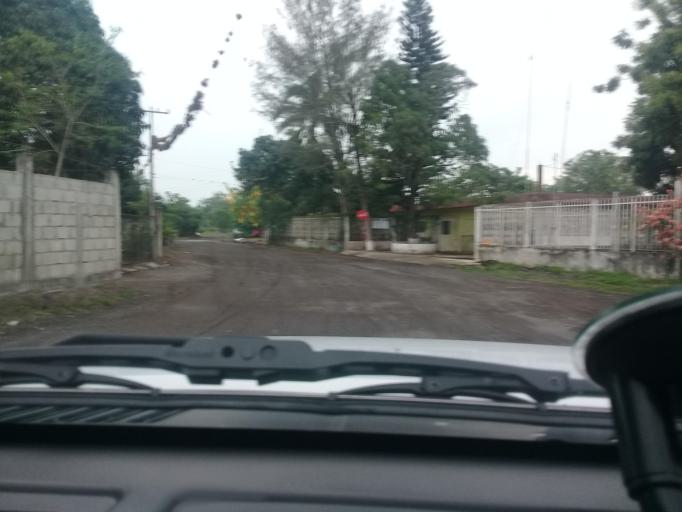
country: MX
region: Veracruz
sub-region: Puente Nacional
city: Cabezas
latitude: 19.3587
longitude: -96.4190
